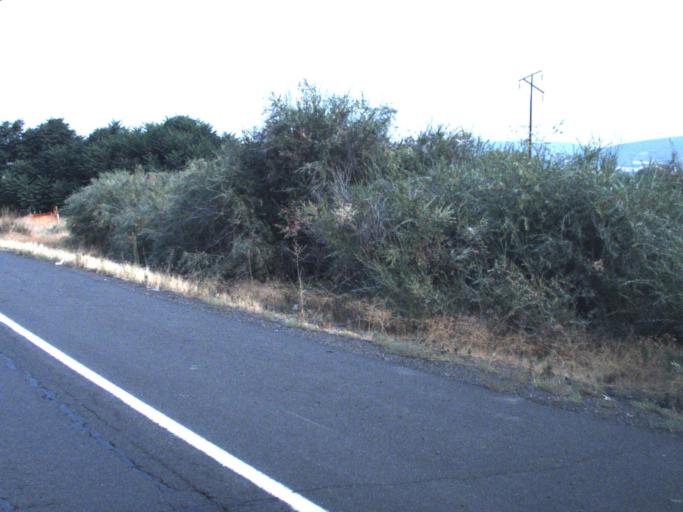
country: US
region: Washington
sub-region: Yakima County
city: Wapato
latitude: 46.4806
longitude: -120.4491
